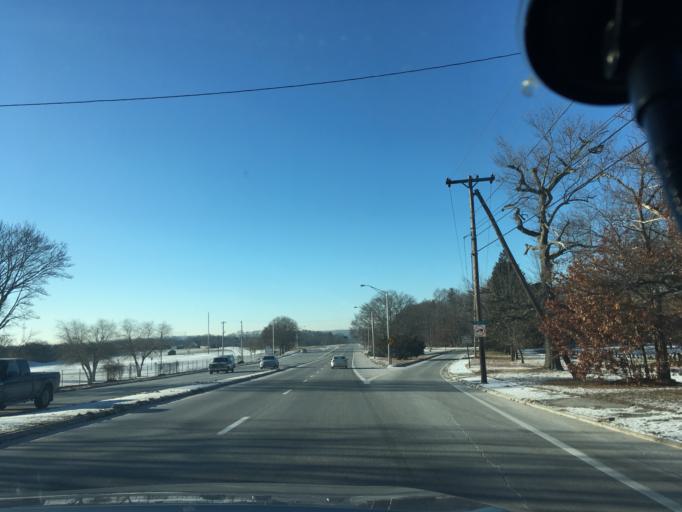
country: US
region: Rhode Island
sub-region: Providence County
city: Cranston
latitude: 41.7469
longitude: -71.4695
